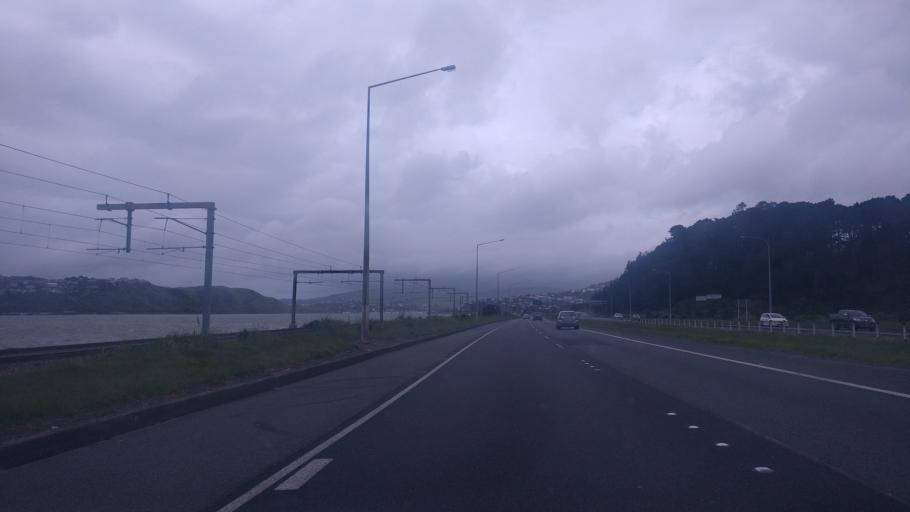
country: NZ
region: Wellington
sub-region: Porirua City
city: Porirua
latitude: -41.1258
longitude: 174.8476
